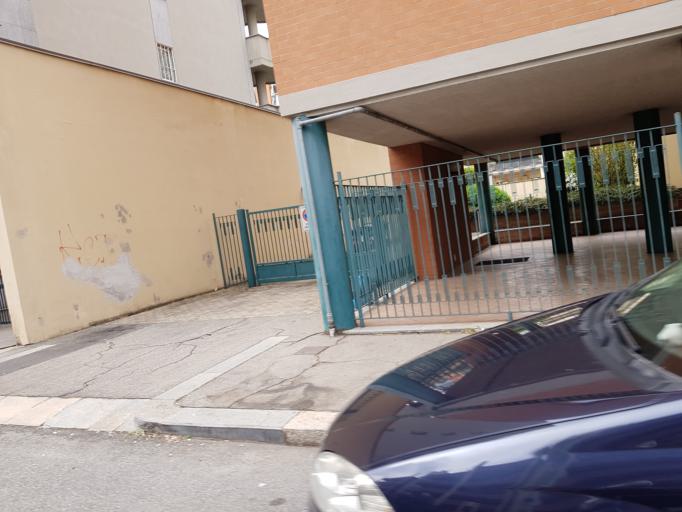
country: IT
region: Piedmont
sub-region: Provincia di Torino
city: Lesna
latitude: 45.0674
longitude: 7.6237
